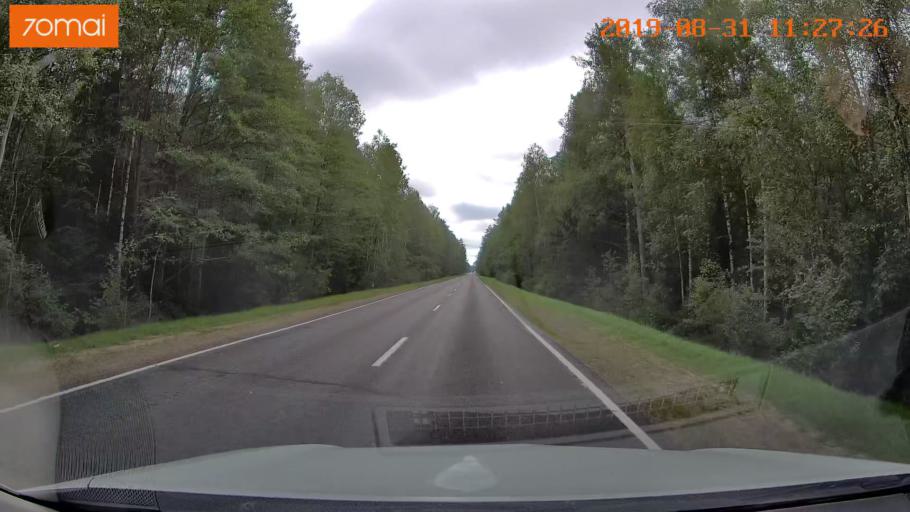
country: BY
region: Mogilev
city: Chavusy
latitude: 53.7516
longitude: 31.0874
